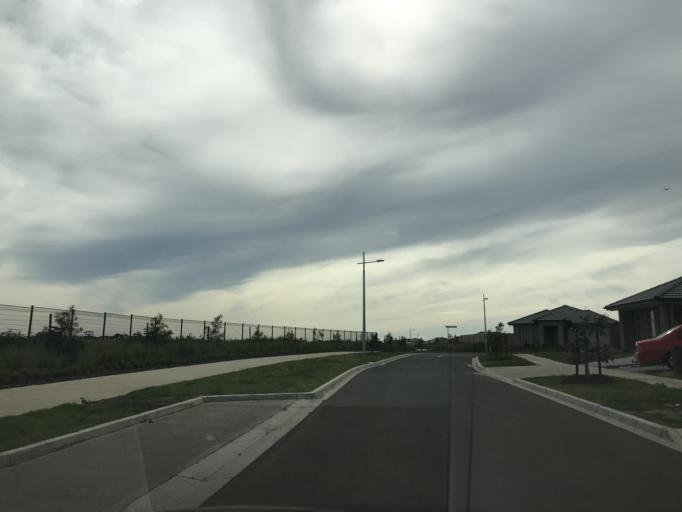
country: AU
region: Victoria
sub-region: Wyndham
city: Truganina
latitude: -37.8321
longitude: 144.7123
